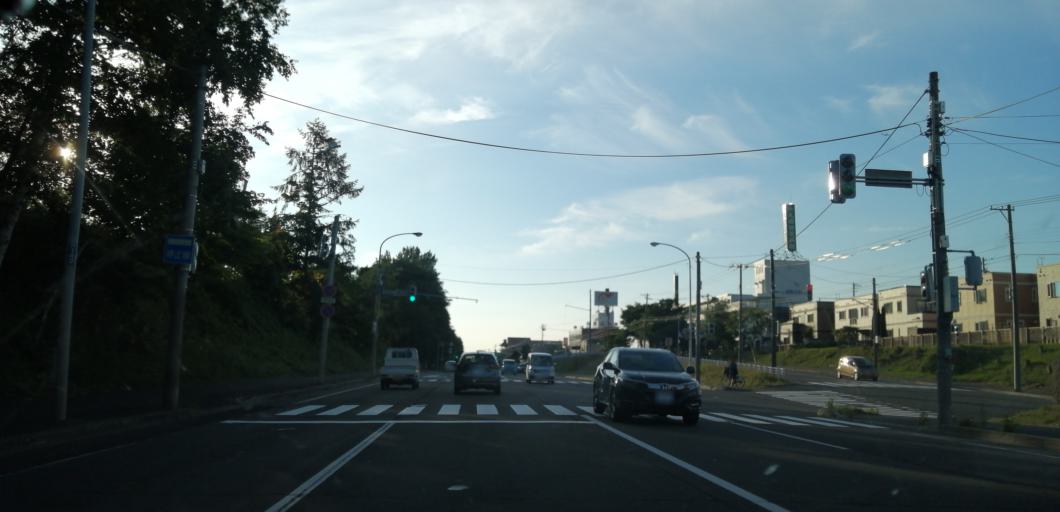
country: JP
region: Hokkaido
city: Sapporo
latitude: 43.0074
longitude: 141.4277
